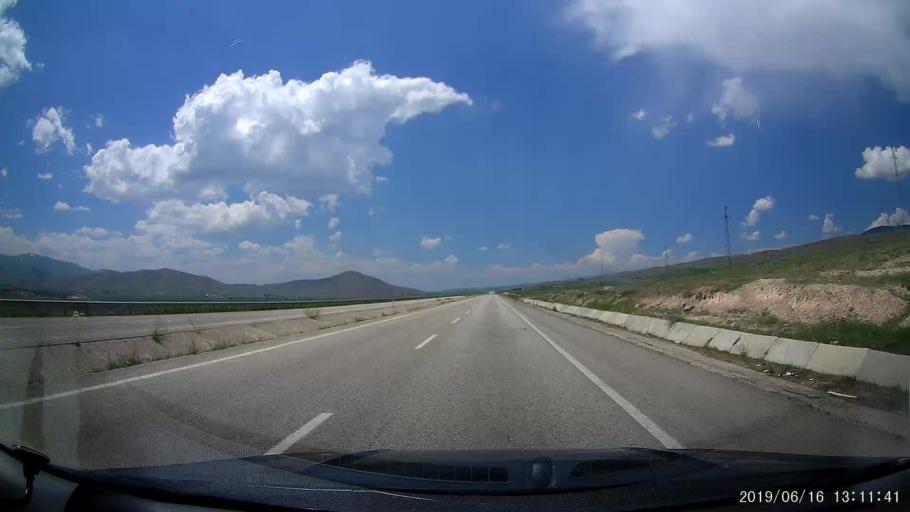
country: TR
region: Agri
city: Diyadin
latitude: 39.5928
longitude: 43.6005
